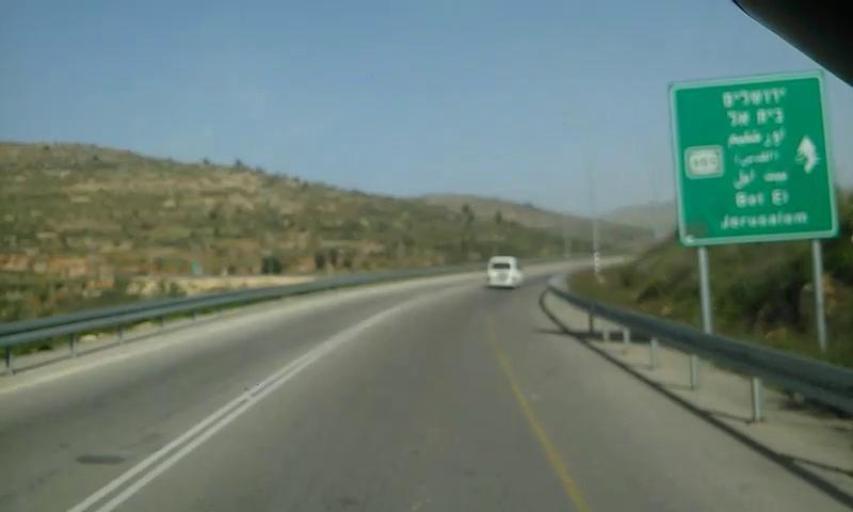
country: PS
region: West Bank
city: `Atarah
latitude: 31.9880
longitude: 35.2273
